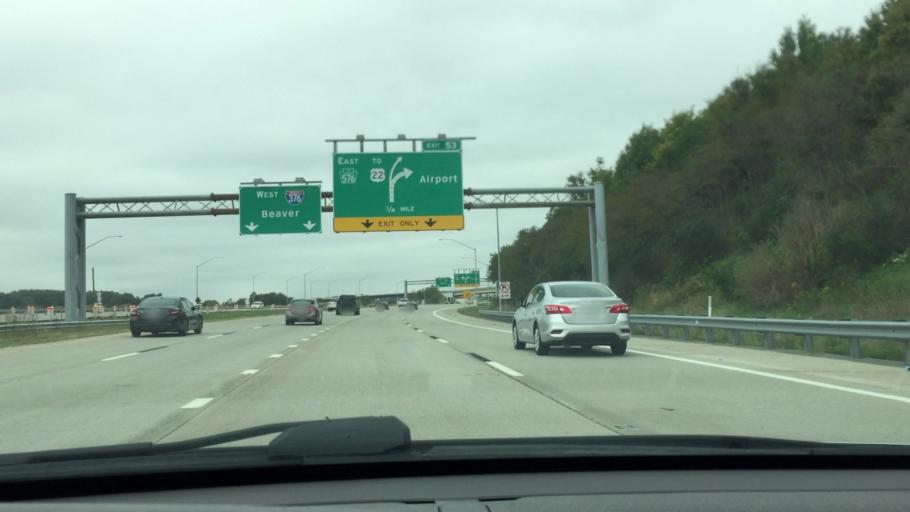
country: US
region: Pennsylvania
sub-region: Allegheny County
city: Imperial
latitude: 40.4823
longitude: -80.2610
